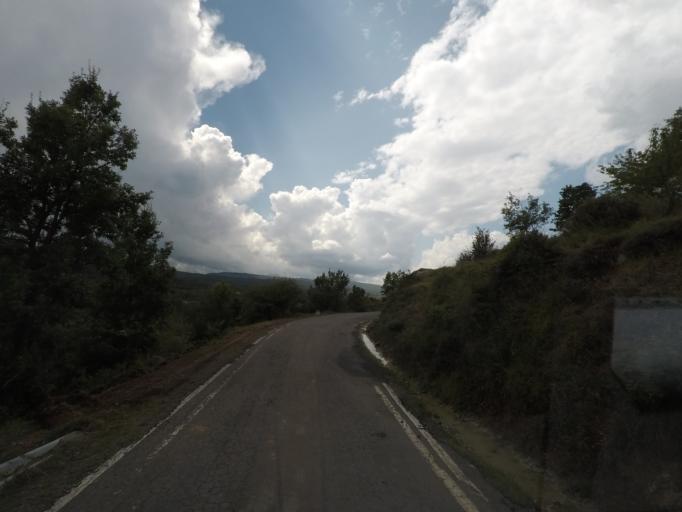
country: ES
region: Aragon
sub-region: Provincia de Huesca
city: Fiscal
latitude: 42.4099
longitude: -0.1099
